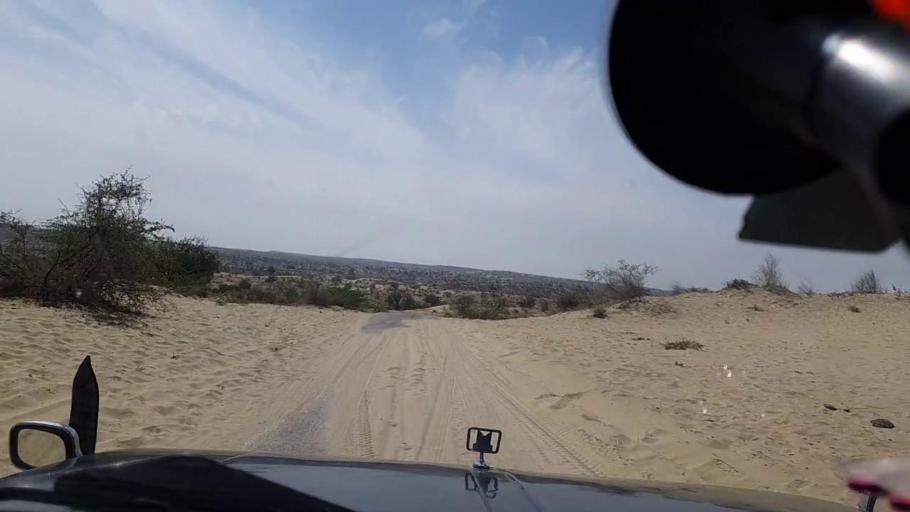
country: PK
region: Sindh
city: Diplo
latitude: 24.4221
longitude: 69.5830
